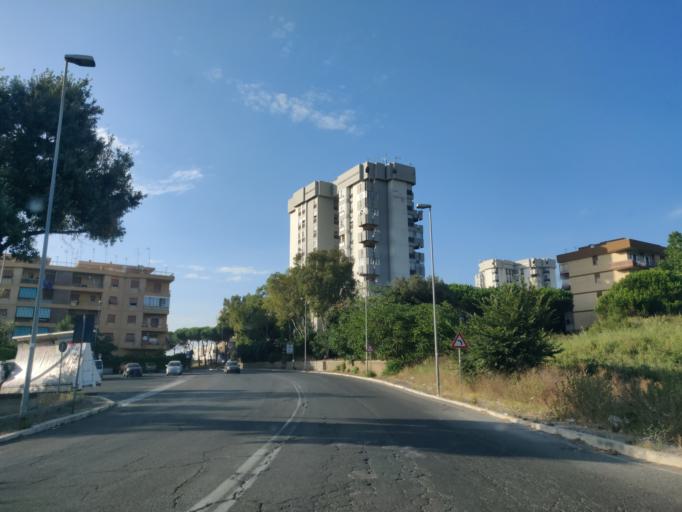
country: IT
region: Latium
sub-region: Citta metropolitana di Roma Capitale
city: Civitavecchia
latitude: 42.0804
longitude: 11.8141
